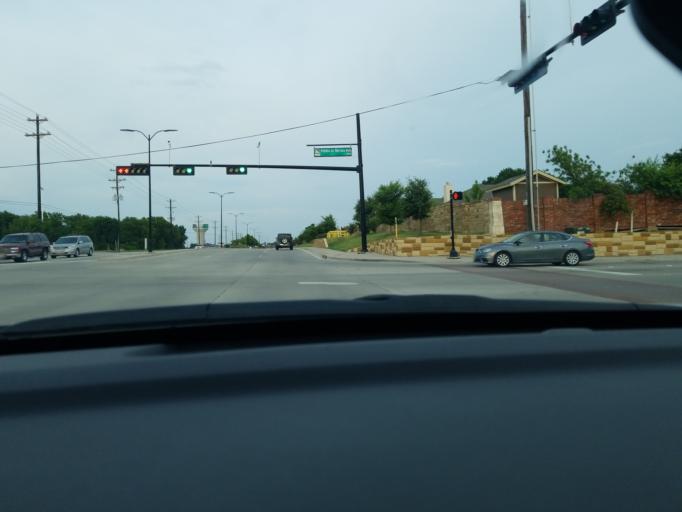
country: US
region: Texas
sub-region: Denton County
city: Little Elm
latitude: 33.1684
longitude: -96.9080
